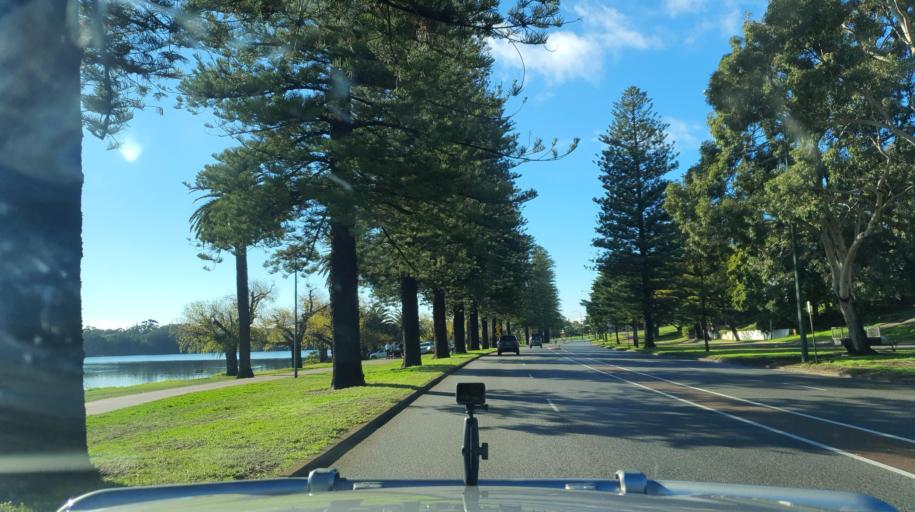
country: AU
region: Western Australia
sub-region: Cambridge
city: West Leederville
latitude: -31.9333
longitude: 115.8275
